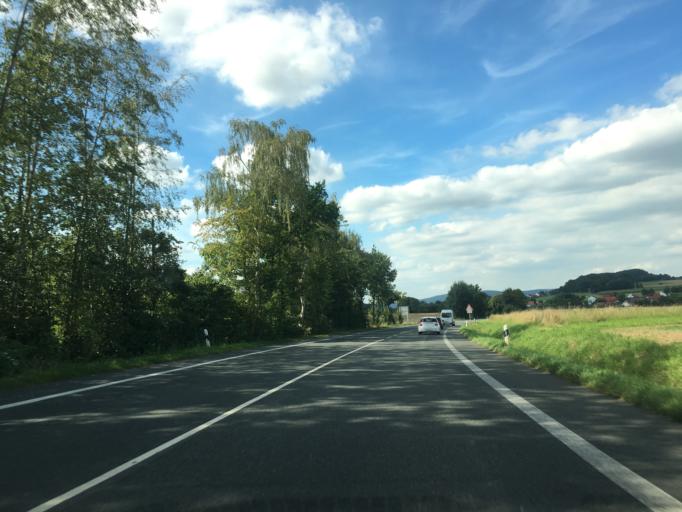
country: DE
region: North Rhine-Westphalia
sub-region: Regierungsbezirk Detmold
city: Dorentrup
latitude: 51.9821
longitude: 9.0055
